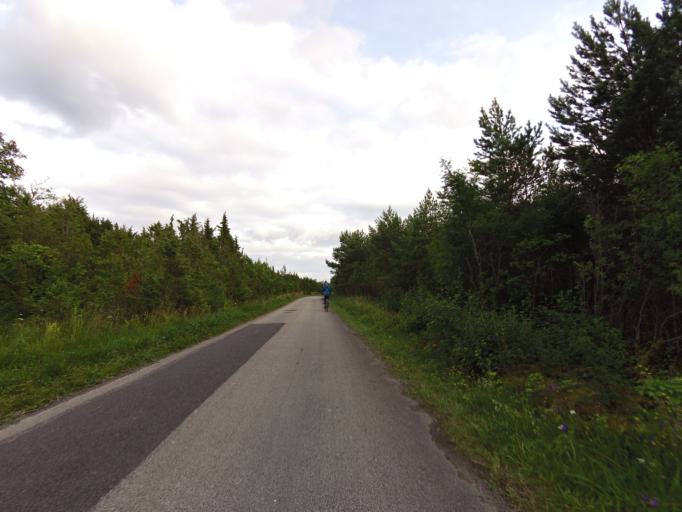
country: EE
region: Laeaene
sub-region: Vormsi vald
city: Hullo
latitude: 58.9747
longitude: 23.2604
